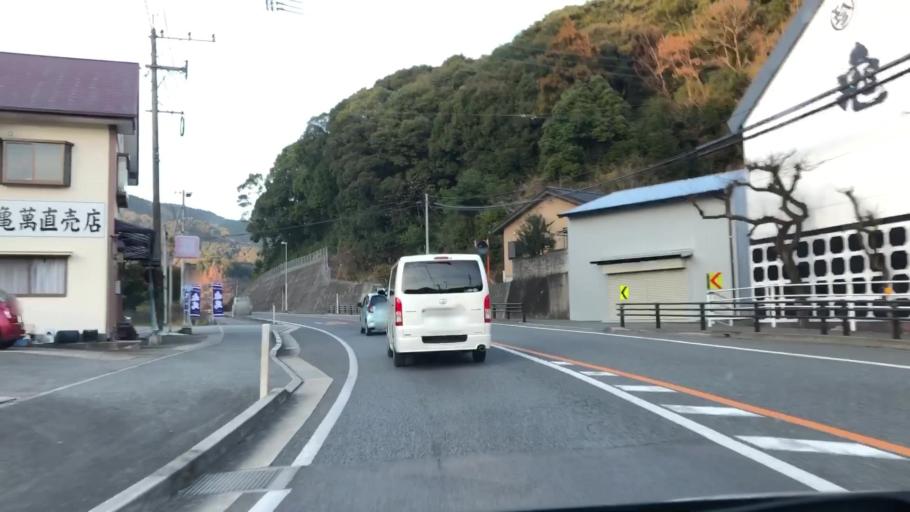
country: JP
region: Kumamoto
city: Minamata
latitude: 32.2351
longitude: 130.4655
